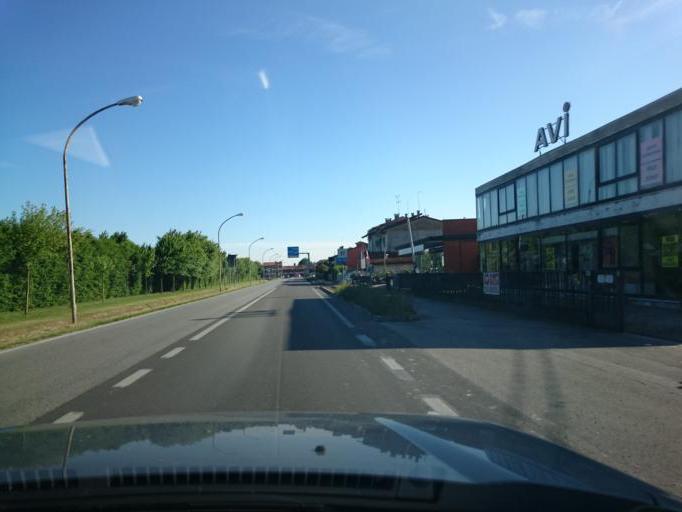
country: IT
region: Veneto
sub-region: Provincia di Venezia
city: Santa Maria di Sala
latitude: 45.5080
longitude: 12.0313
